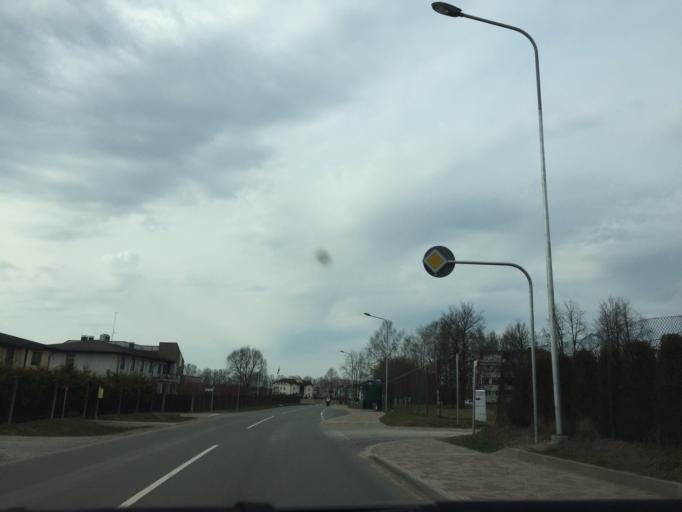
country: LV
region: Kekava
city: Balozi
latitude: 56.8857
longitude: 24.1604
